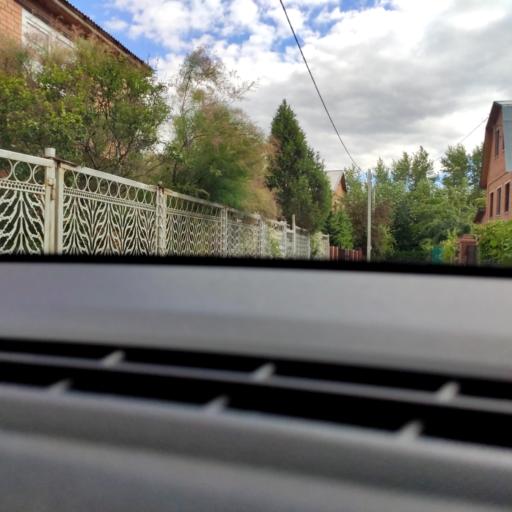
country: RU
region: Samara
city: Podstepki
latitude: 53.5780
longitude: 49.0737
